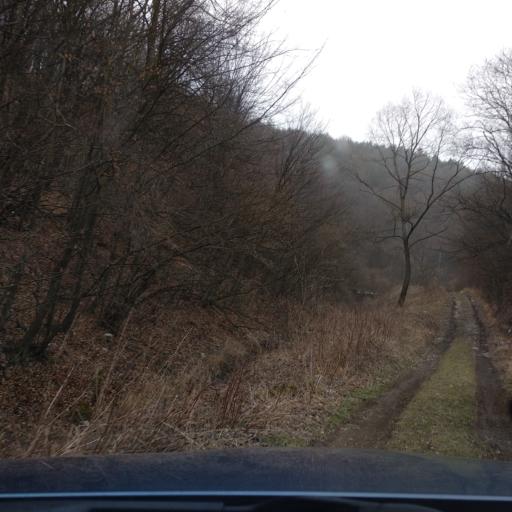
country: SK
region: Nitriansky
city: Ilava
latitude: 48.9167
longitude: 18.3093
